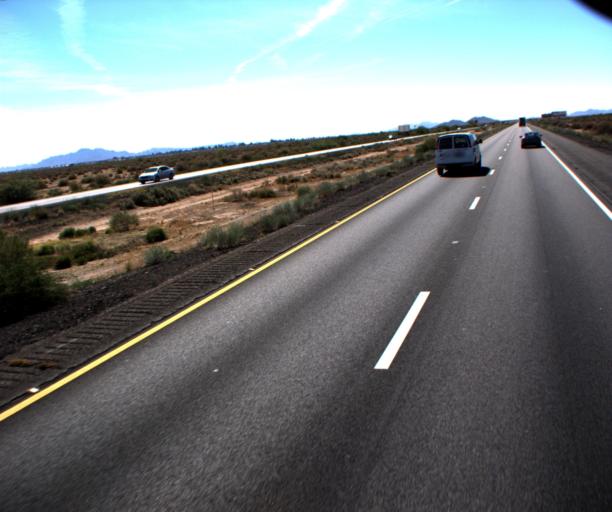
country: US
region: Arizona
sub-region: Maricopa County
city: Sun Lakes
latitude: 33.2333
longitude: -111.9313
